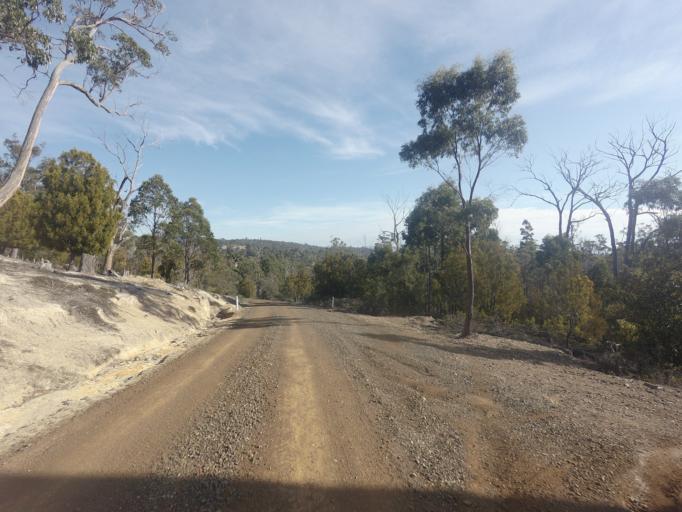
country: AU
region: Tasmania
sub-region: Sorell
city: Sorell
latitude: -42.5292
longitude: 147.4540
